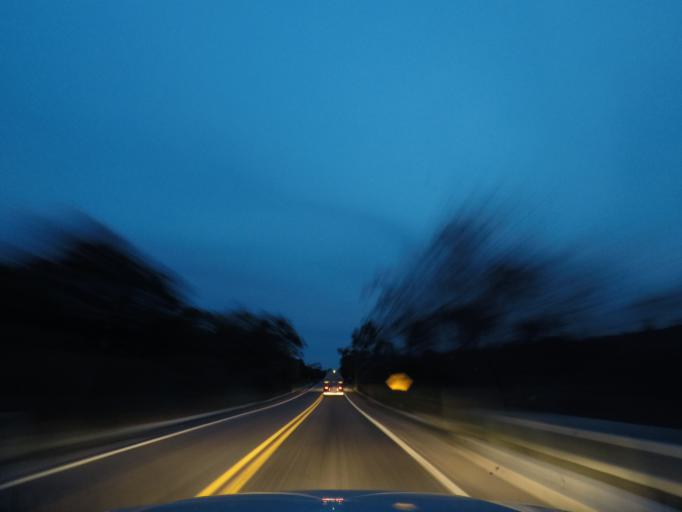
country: BR
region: Bahia
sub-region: Andarai
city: Vera Cruz
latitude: -12.4946
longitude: -41.3281
